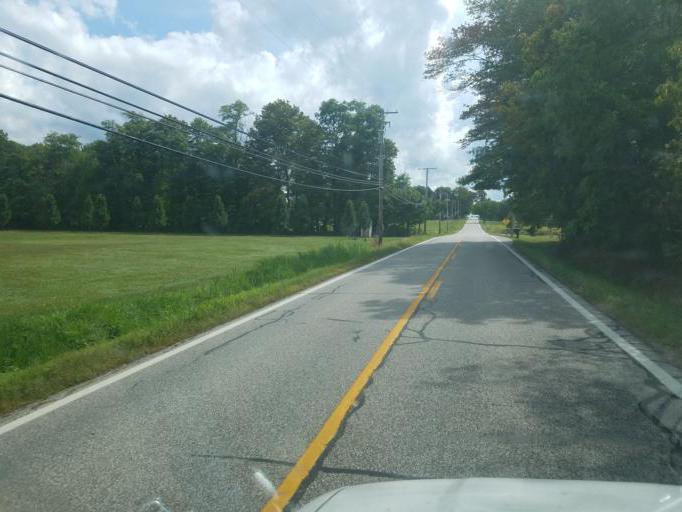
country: US
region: Ohio
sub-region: Geauga County
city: Burton
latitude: 41.3930
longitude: -81.1438
